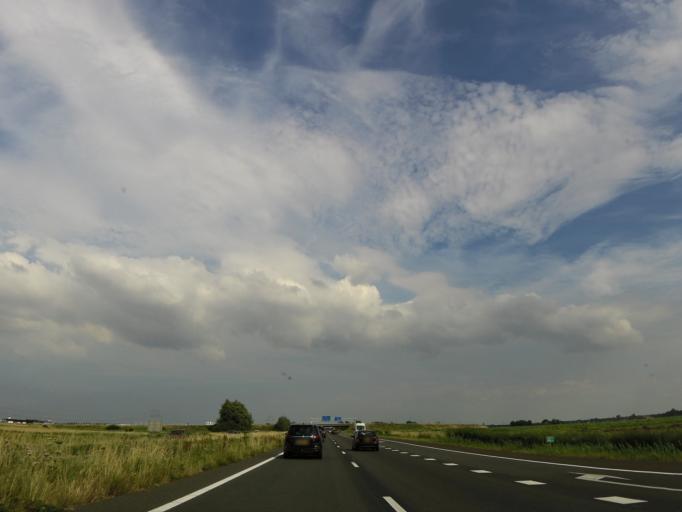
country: NL
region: Zeeland
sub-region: Gemeente Goes
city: Goes
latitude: 51.4836
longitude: 3.8634
